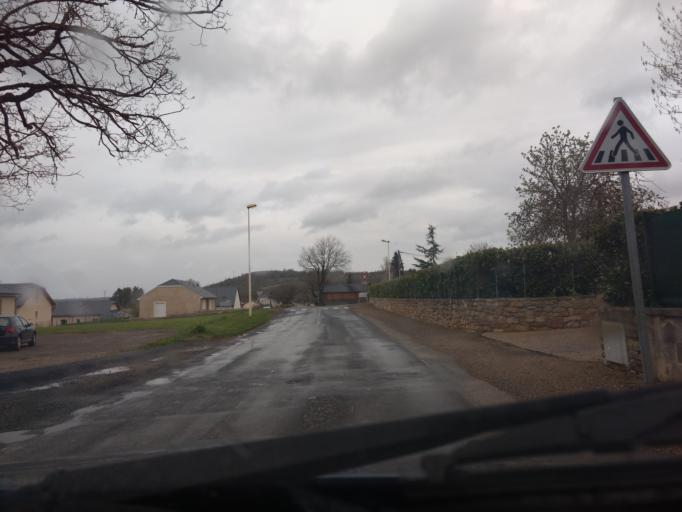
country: FR
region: Midi-Pyrenees
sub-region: Departement de l'Aveyron
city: La Loubiere
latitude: 44.3982
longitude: 2.6960
